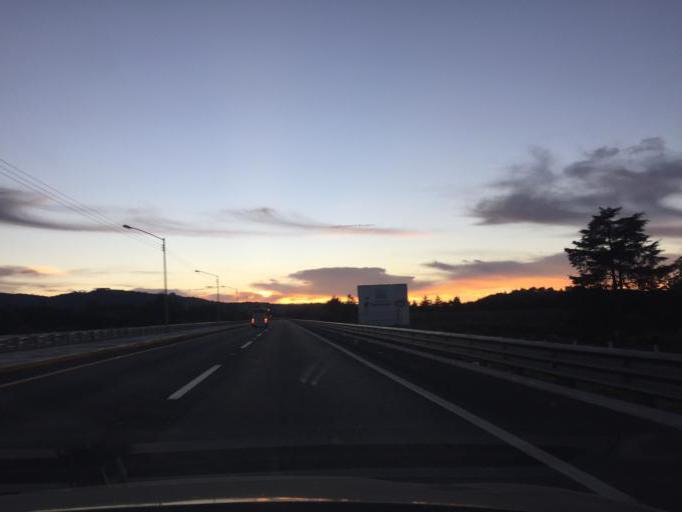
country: MX
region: Puebla
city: San Jose Esperanza
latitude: 18.8618
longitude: -97.3667
